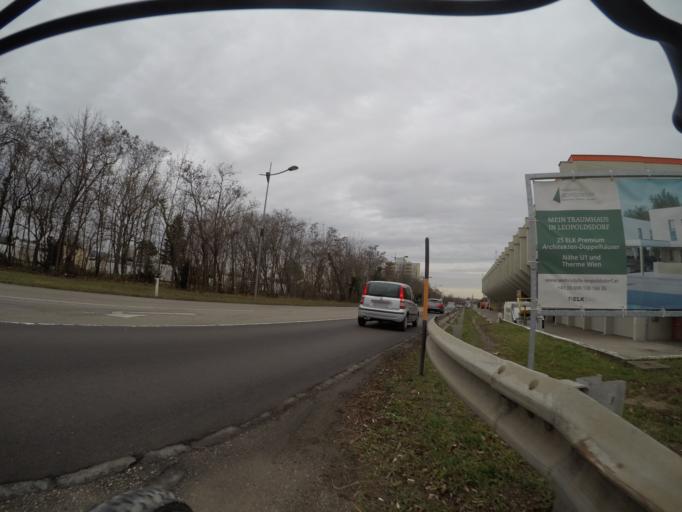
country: AT
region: Lower Austria
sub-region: Politischer Bezirk Modling
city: Wiener Neudorf
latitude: 48.0971
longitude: 16.3104
